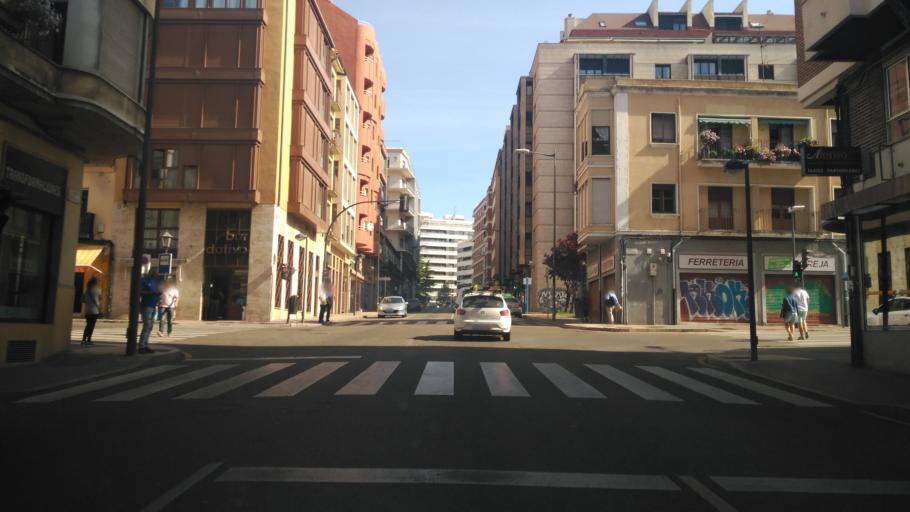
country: ES
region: Castille and Leon
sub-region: Provincia de Zamora
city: Zamora
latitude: 41.5042
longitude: -5.7399
